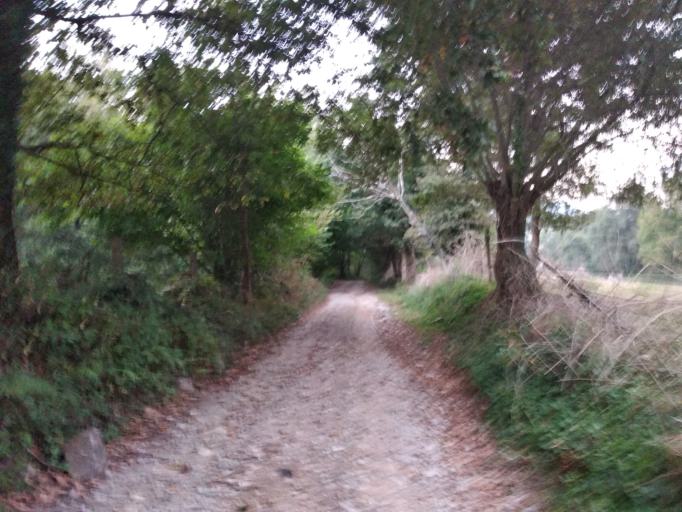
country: ES
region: Cantabria
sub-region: Provincia de Cantabria
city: Entrambasaguas
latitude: 43.3332
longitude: -3.6802
